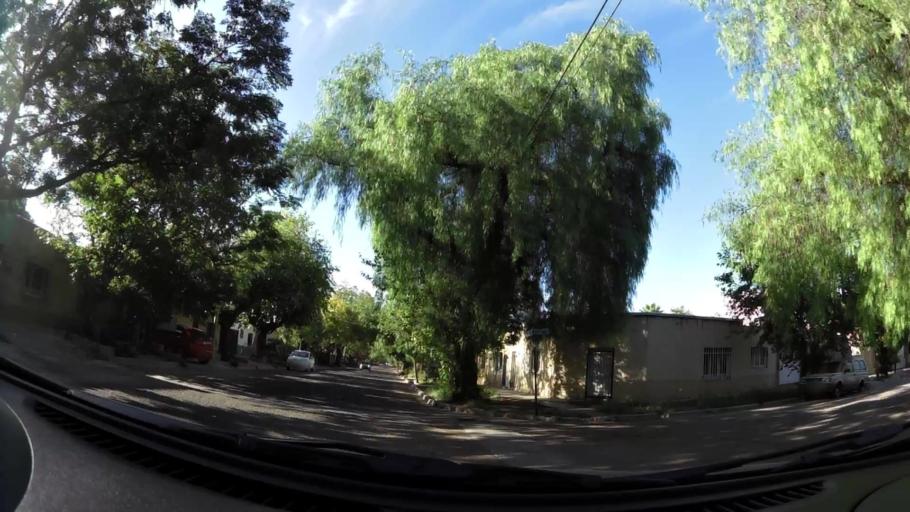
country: AR
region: Mendoza
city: Mendoza
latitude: -32.9034
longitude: -68.8213
